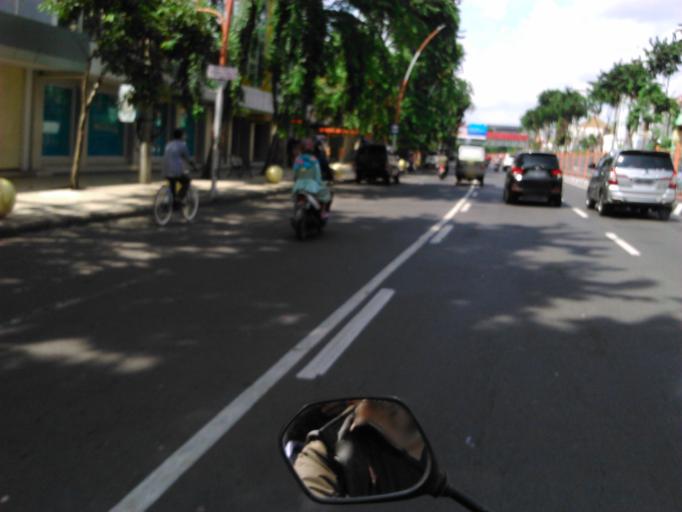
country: ID
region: East Java
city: Gubengairlangga
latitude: -7.2746
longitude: 112.7419
